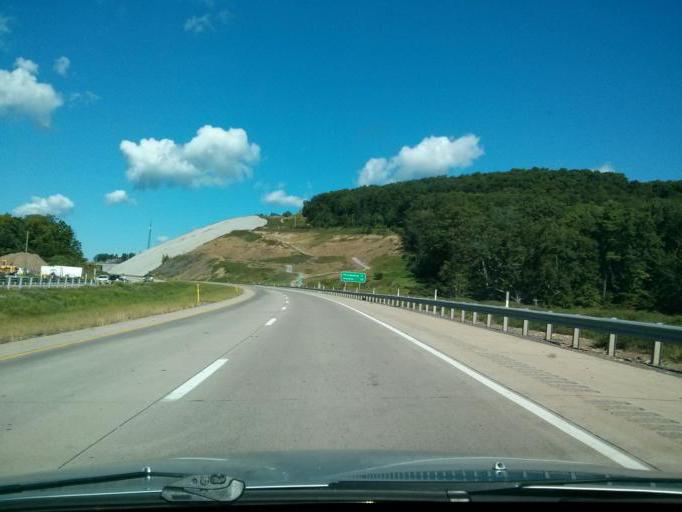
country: US
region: Pennsylvania
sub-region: Centre County
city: Park Forest Village
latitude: 40.8303
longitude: -77.9583
